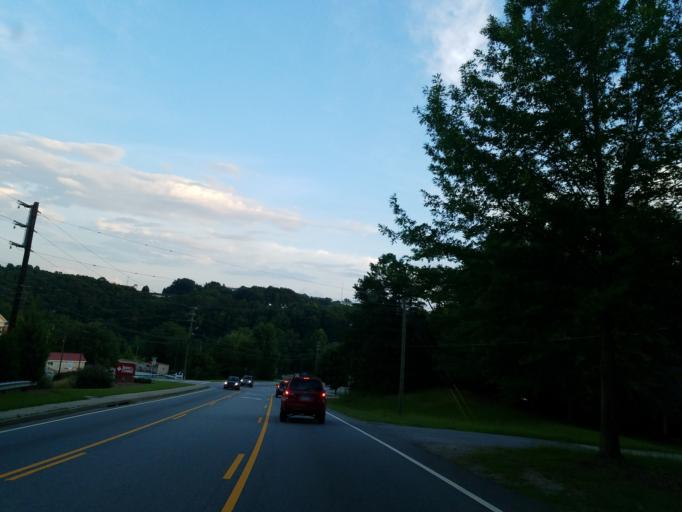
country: US
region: Georgia
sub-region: Lumpkin County
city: Dahlonega
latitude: 34.5312
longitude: -83.9778
